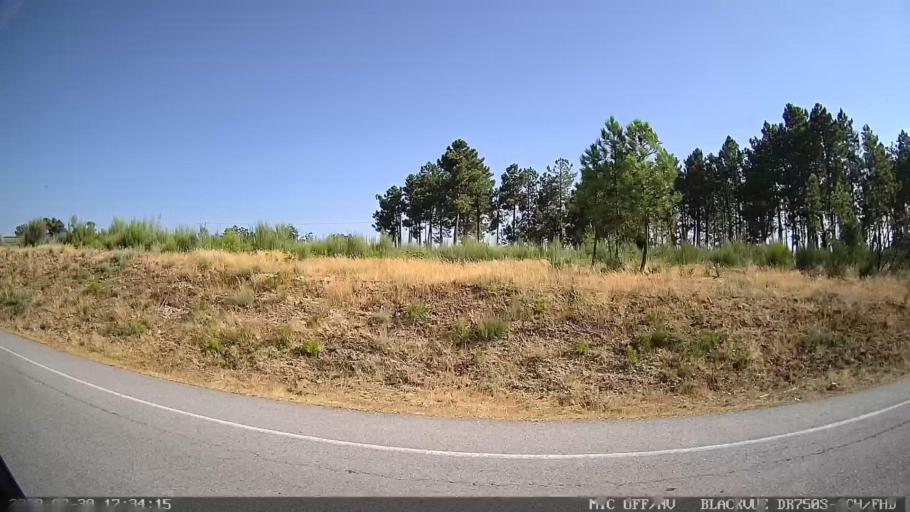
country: PT
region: Vila Real
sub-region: Murca
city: Murca
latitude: 41.3530
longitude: -7.4817
